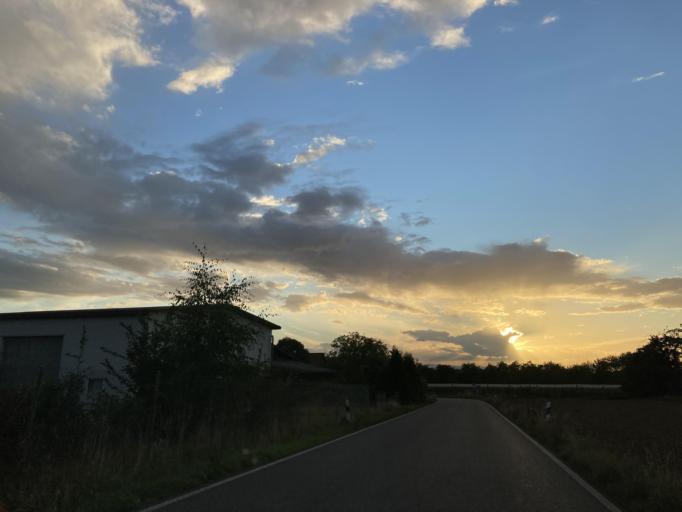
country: DE
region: Baden-Wuerttemberg
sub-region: Freiburg Region
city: Lauf
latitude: 48.6663
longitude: 8.1329
